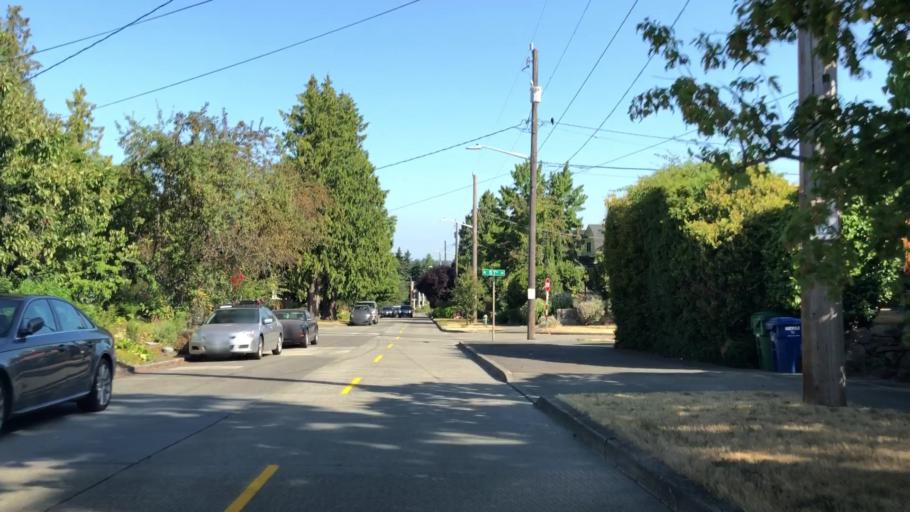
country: US
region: Washington
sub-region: King County
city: Seattle
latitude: 47.6696
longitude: -122.3322
